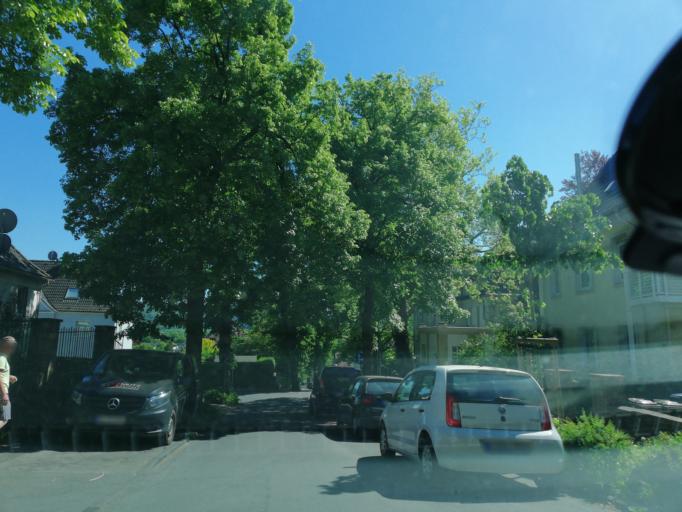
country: DE
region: North Rhine-Westphalia
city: Wetter (Ruhr)
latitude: 51.3859
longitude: 7.3930
